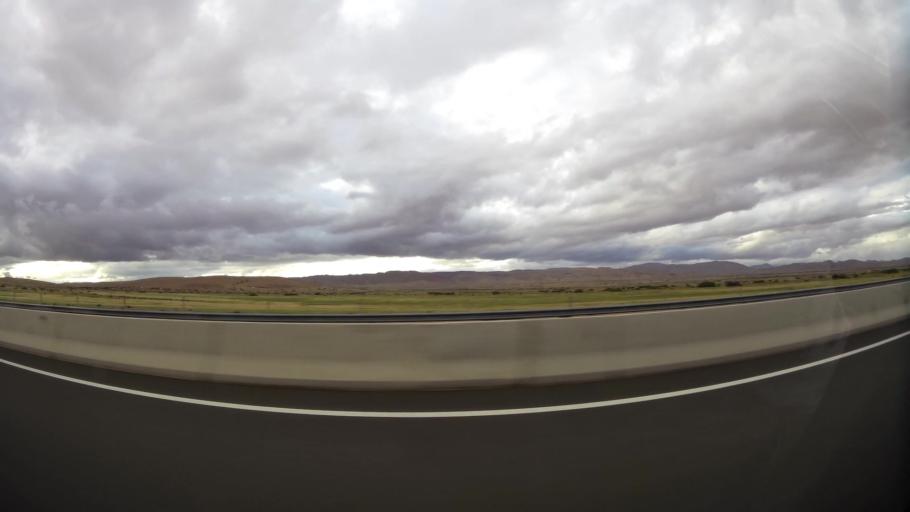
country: MA
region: Taza-Al Hoceima-Taounate
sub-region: Taza
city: Guercif
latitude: 34.3050
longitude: -3.6520
